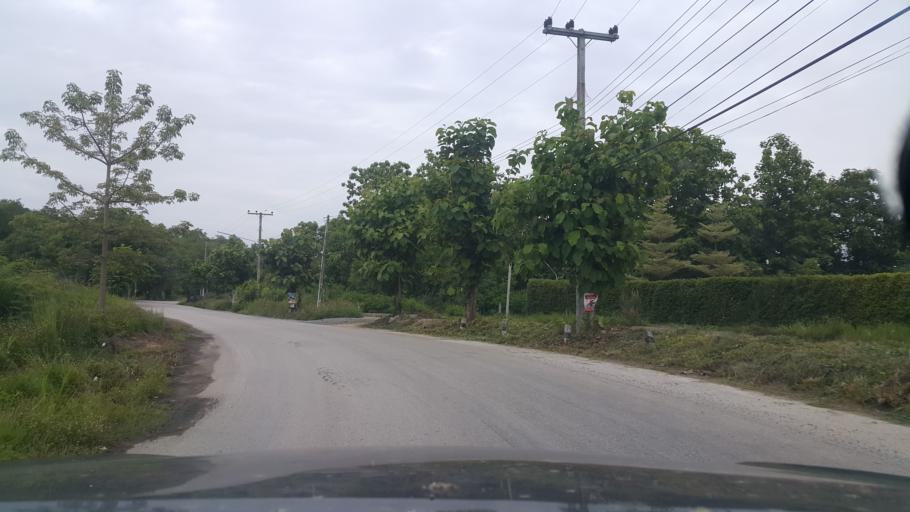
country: TH
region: Chiang Mai
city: San Pa Tong
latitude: 18.6635
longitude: 98.8351
